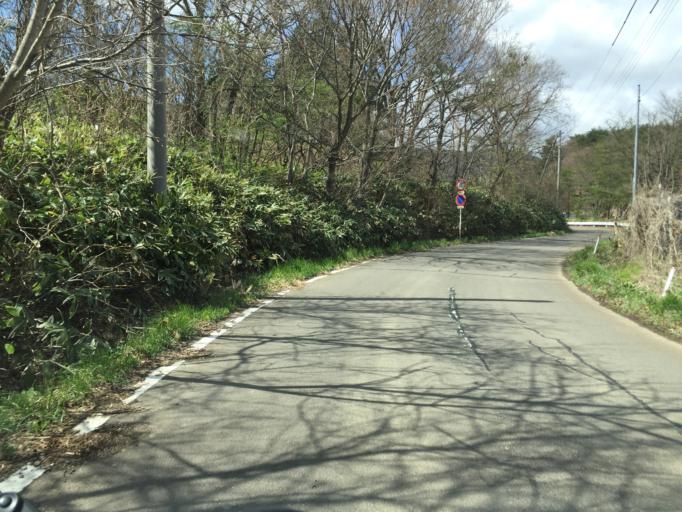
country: JP
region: Fukushima
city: Fukushima-shi
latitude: 37.8318
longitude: 140.4264
